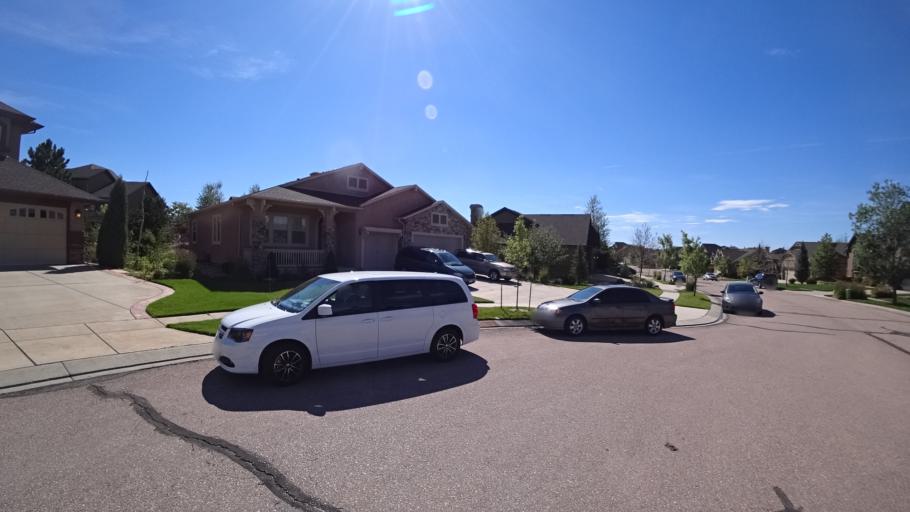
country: US
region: Colorado
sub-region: El Paso County
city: Gleneagle
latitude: 39.0264
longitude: -104.8033
